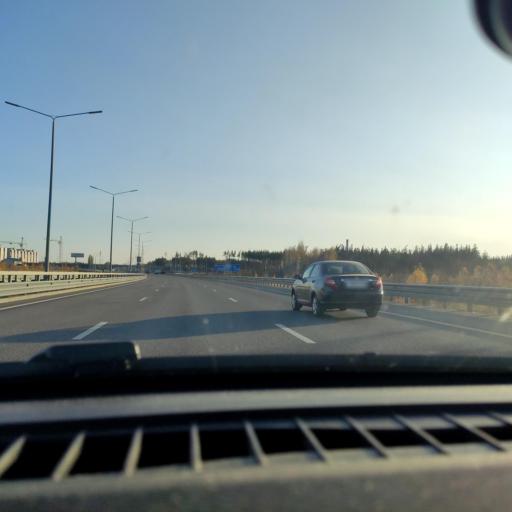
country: RU
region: Voronezj
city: Somovo
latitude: 51.7475
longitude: 39.3058
